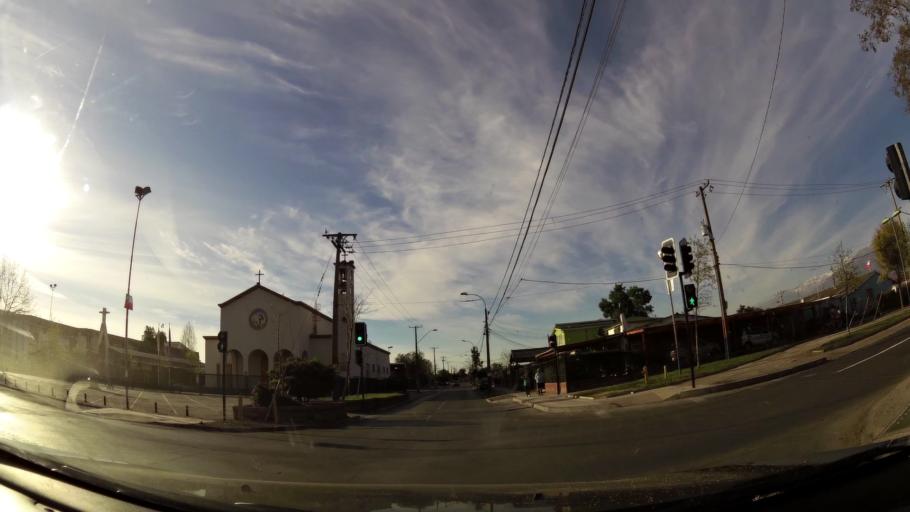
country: CL
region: Santiago Metropolitan
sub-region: Provincia de Cordillera
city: Puente Alto
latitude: -33.6168
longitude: -70.5779
